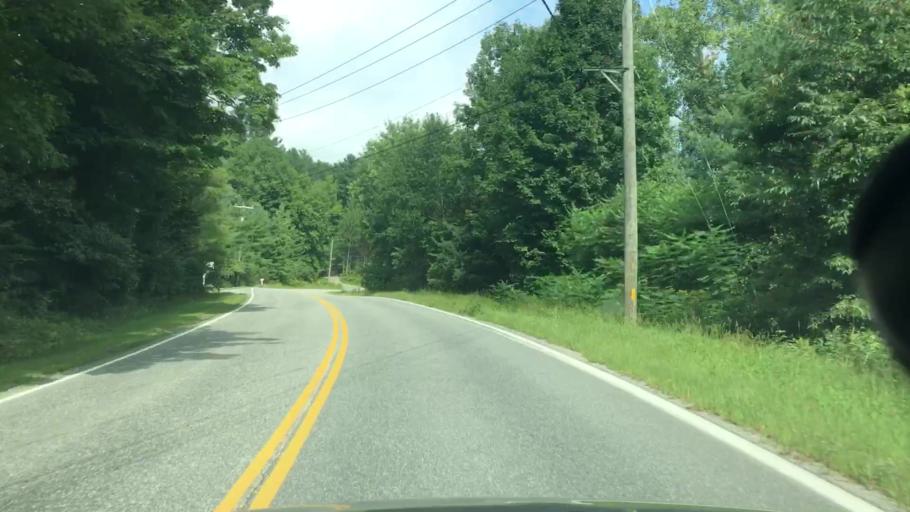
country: US
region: Massachusetts
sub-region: Franklin County
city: Colrain
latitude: 42.6354
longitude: -72.6673
